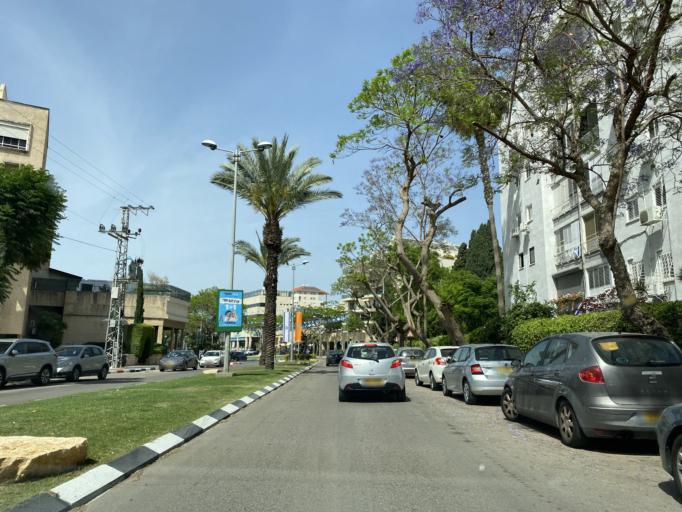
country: IL
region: Central District
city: Ra'anana
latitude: 32.1793
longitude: 34.8711
